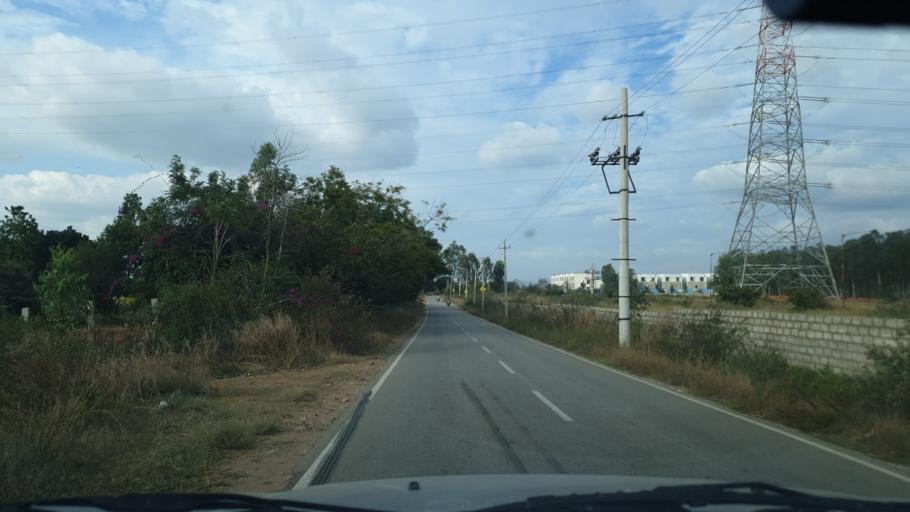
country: IN
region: Karnataka
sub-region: Bangalore Urban
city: Yelahanka
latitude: 13.1998
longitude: 77.6026
